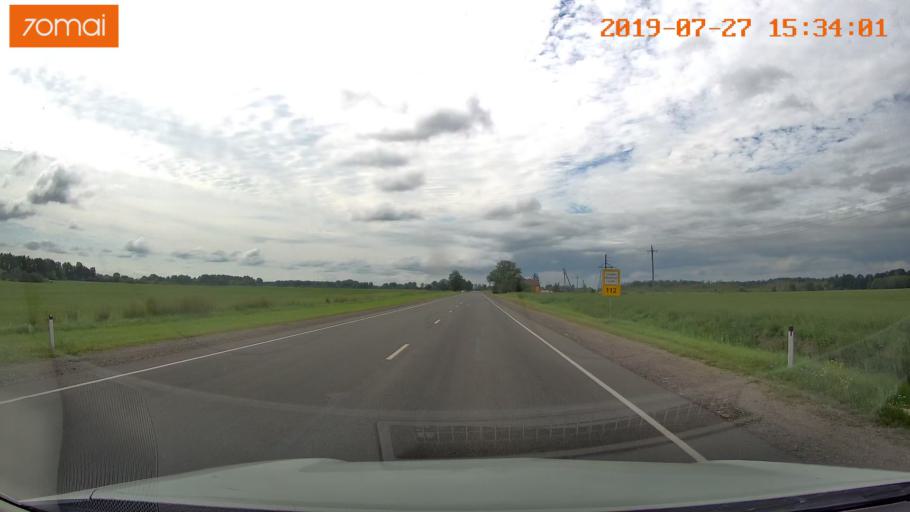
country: RU
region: Kaliningrad
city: Nesterov
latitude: 54.6121
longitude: 22.4358
